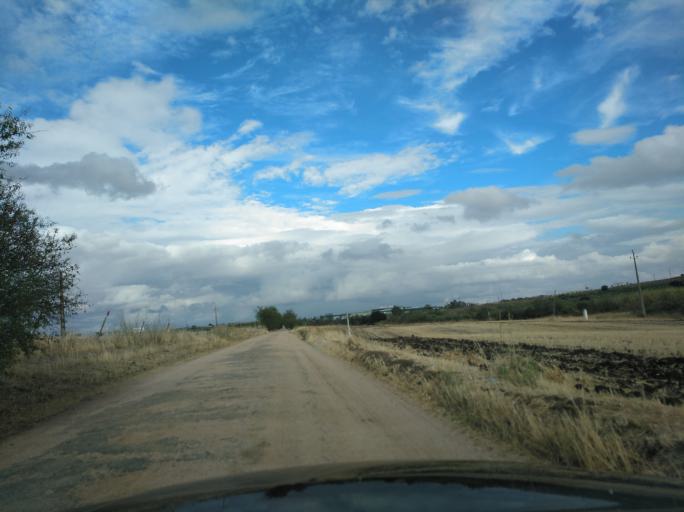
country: PT
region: Portalegre
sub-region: Campo Maior
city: Campo Maior
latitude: 39.0401
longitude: -7.1100
